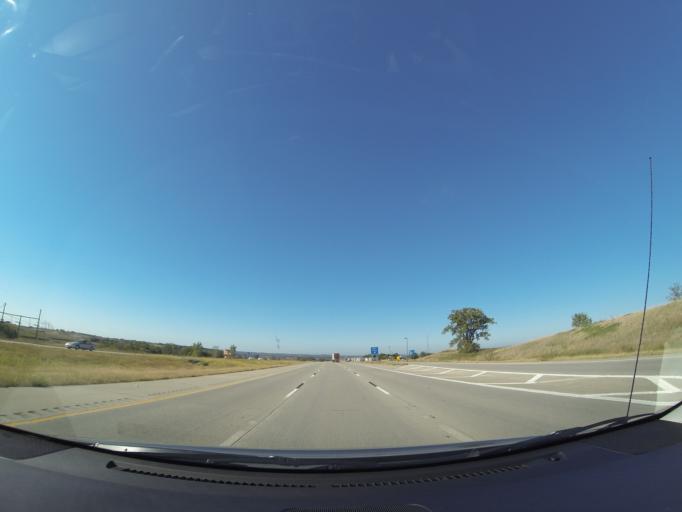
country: US
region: Nebraska
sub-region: Sarpy County
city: Gretna
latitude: 41.0860
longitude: -96.2709
